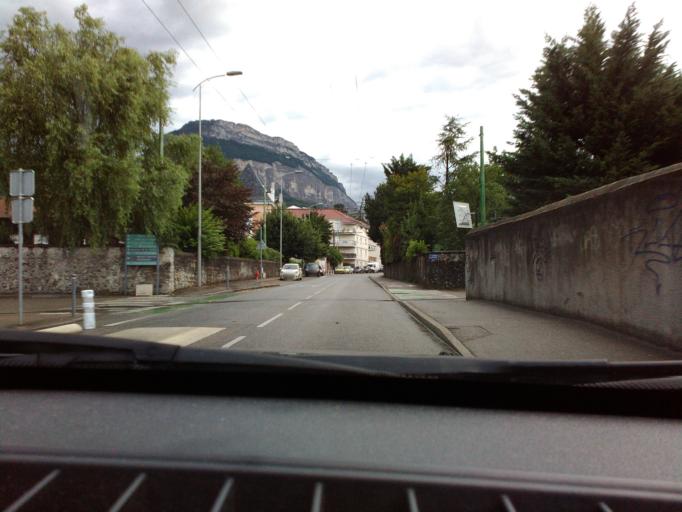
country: FR
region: Rhone-Alpes
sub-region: Departement de l'Isere
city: La Tronche
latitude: 45.2038
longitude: 5.7461
